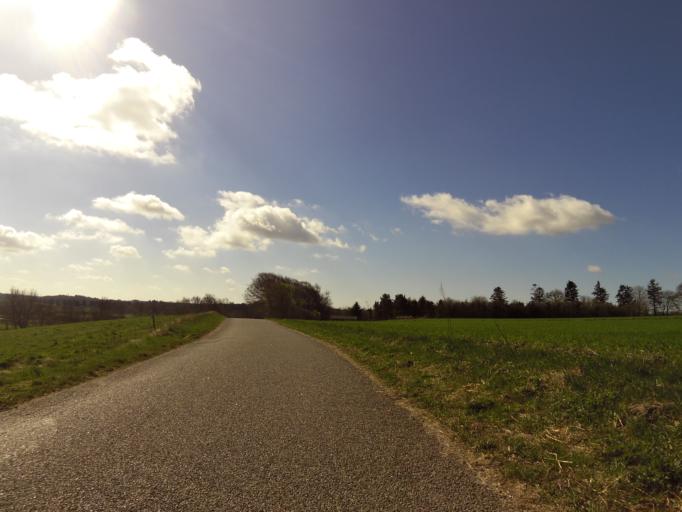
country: DK
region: Central Jutland
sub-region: Holstebro Kommune
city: Vinderup
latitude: 56.4302
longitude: 8.7324
